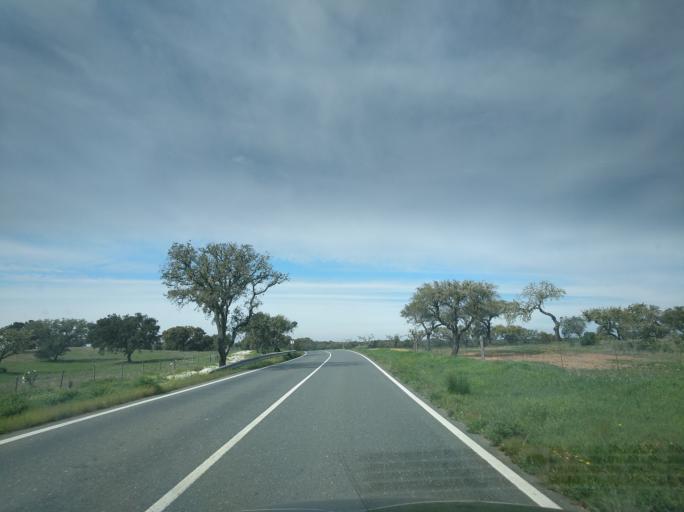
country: PT
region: Beja
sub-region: Mertola
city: Mertola
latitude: 37.7490
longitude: -7.8010
